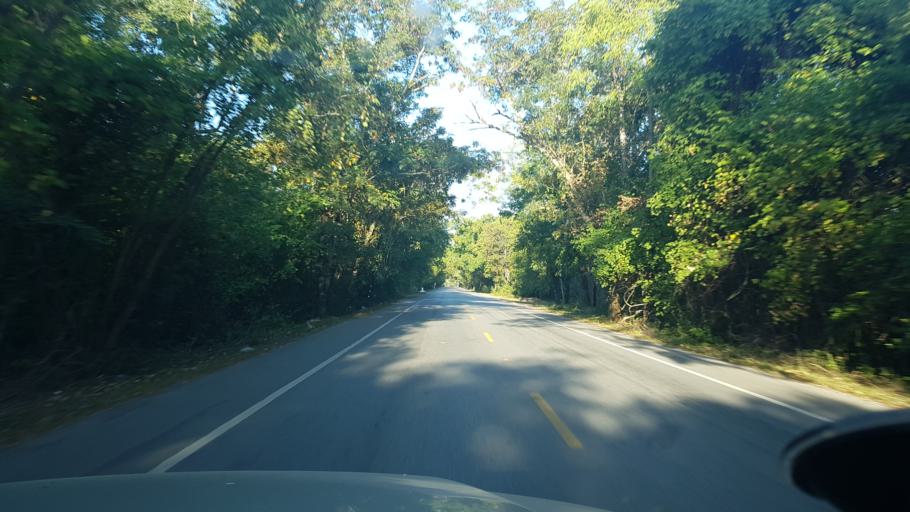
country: TH
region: Khon Kaen
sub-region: Amphoe Phu Pha Man
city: Phu Pha Man
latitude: 16.6213
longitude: 101.8646
